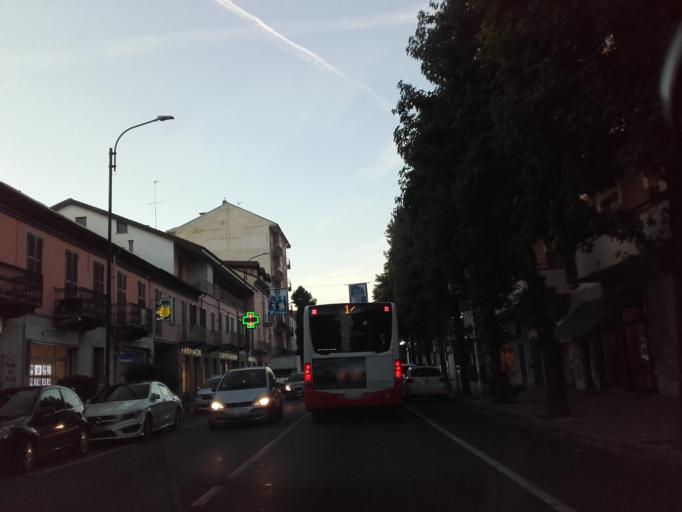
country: IT
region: Piedmont
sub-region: Provincia di Asti
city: Asti
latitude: 44.8907
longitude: 8.2109
